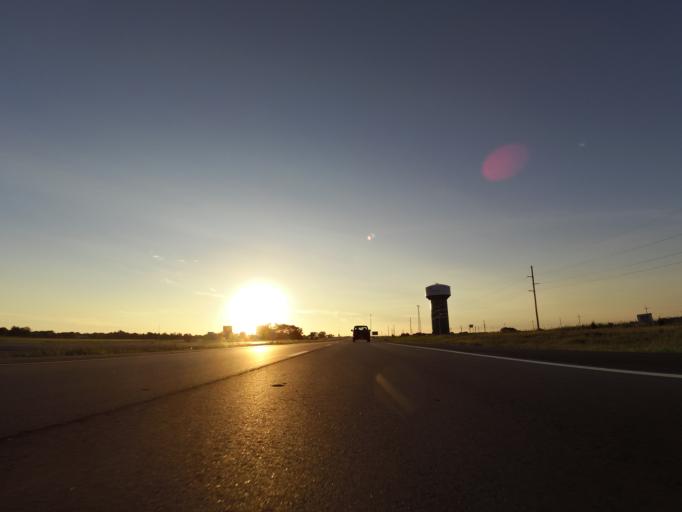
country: US
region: Kansas
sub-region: Reno County
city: South Hutchinson
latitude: 38.0130
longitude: -97.9480
